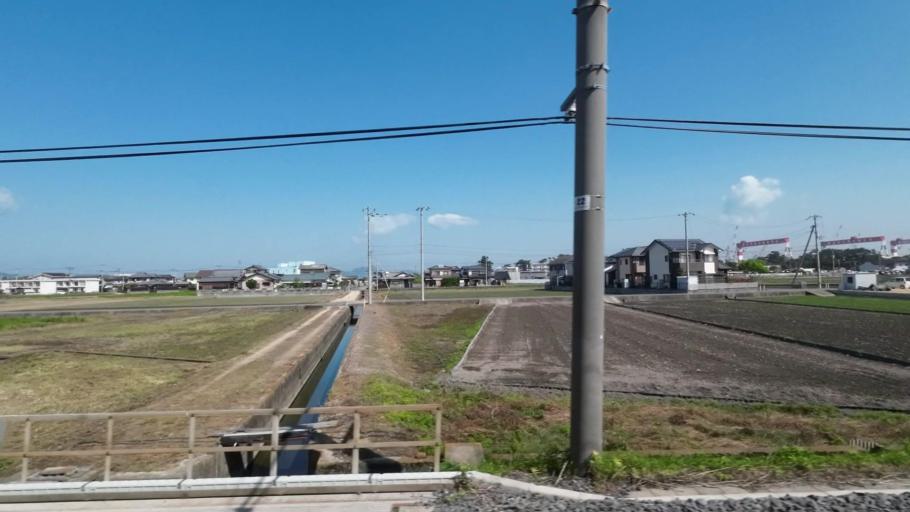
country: JP
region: Kagawa
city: Tadotsu
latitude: 34.2809
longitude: 133.7659
